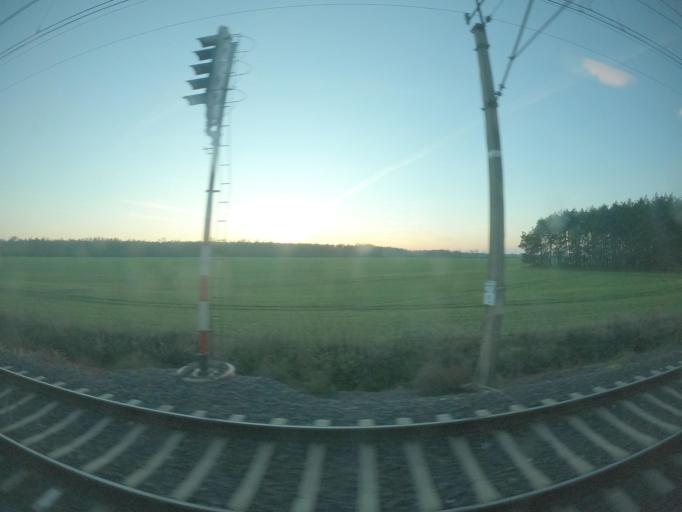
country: PL
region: West Pomeranian Voivodeship
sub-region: Powiat mysliborski
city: Boleszkowice
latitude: 52.7313
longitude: 14.5221
